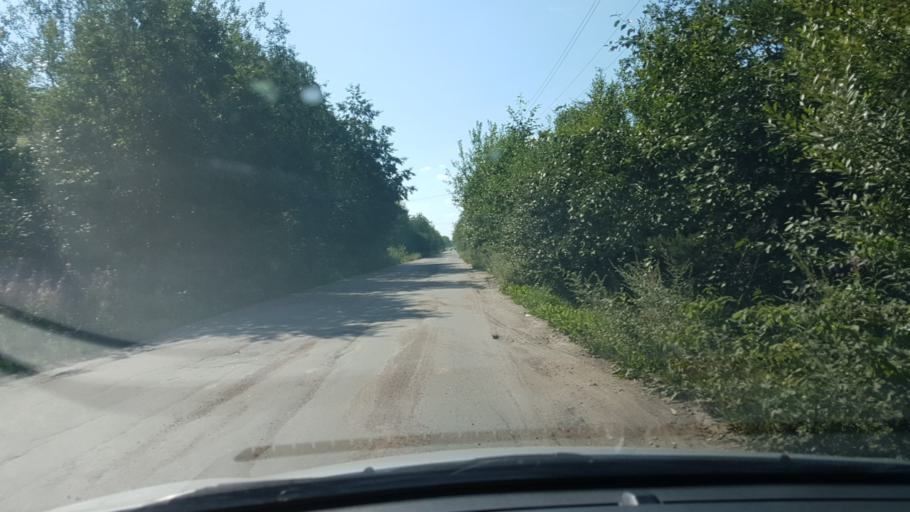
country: RU
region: Leningrad
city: Vyritsa
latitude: 59.4483
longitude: 30.2994
